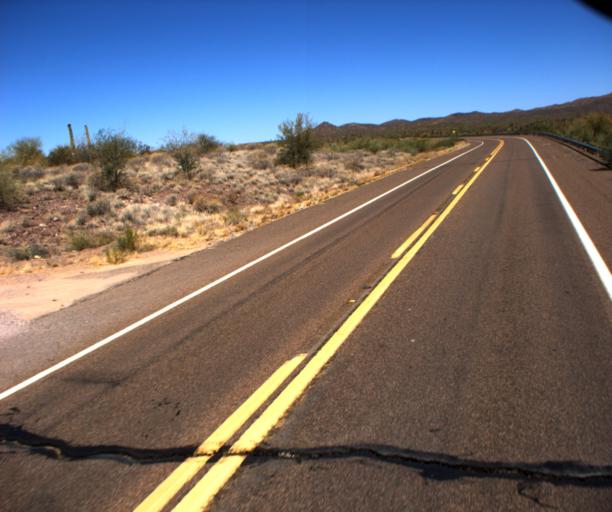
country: US
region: Arizona
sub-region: Pima County
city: Sells
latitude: 32.1638
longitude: -112.1161
